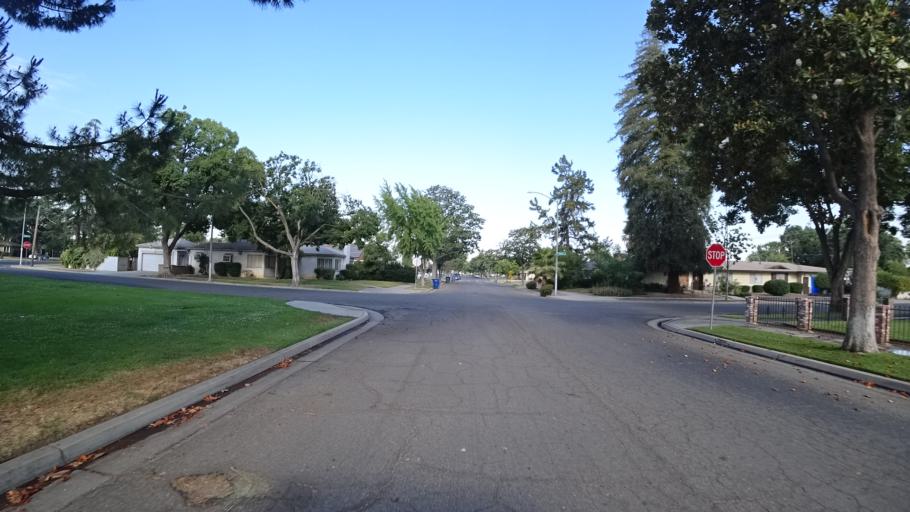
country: US
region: California
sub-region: Fresno County
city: West Park
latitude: 36.7244
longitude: -119.8116
